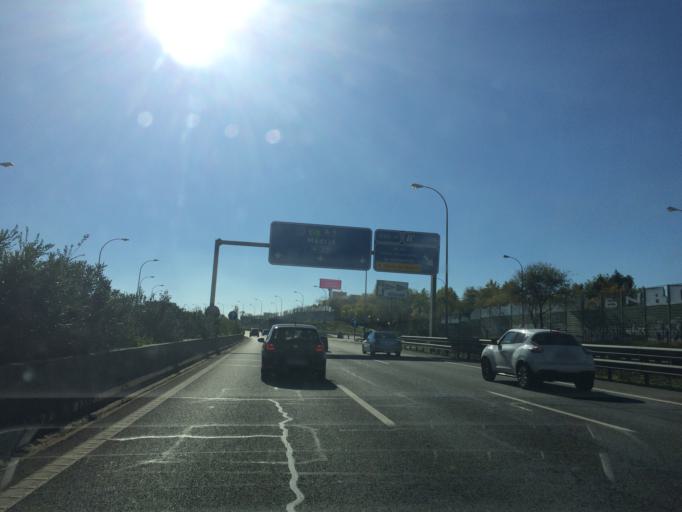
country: ES
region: Madrid
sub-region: Provincia de Madrid
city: Las Tablas
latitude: 40.5222
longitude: -3.6513
